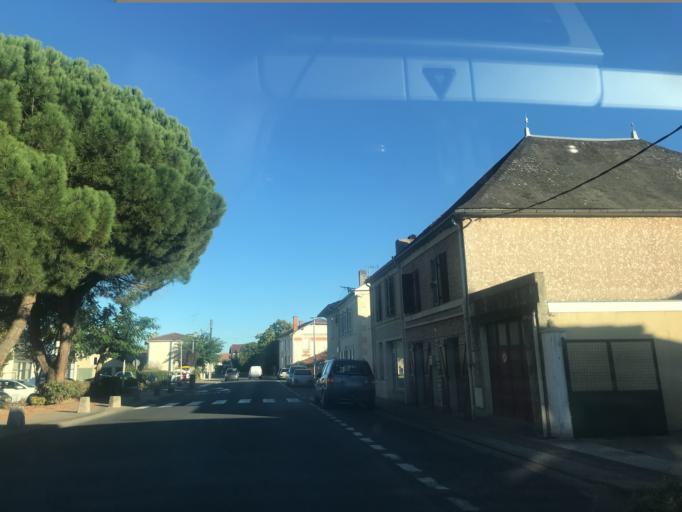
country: FR
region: Poitou-Charentes
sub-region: Departement de la Charente-Maritime
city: Saint-Aigulin
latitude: 45.1598
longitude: -0.0175
